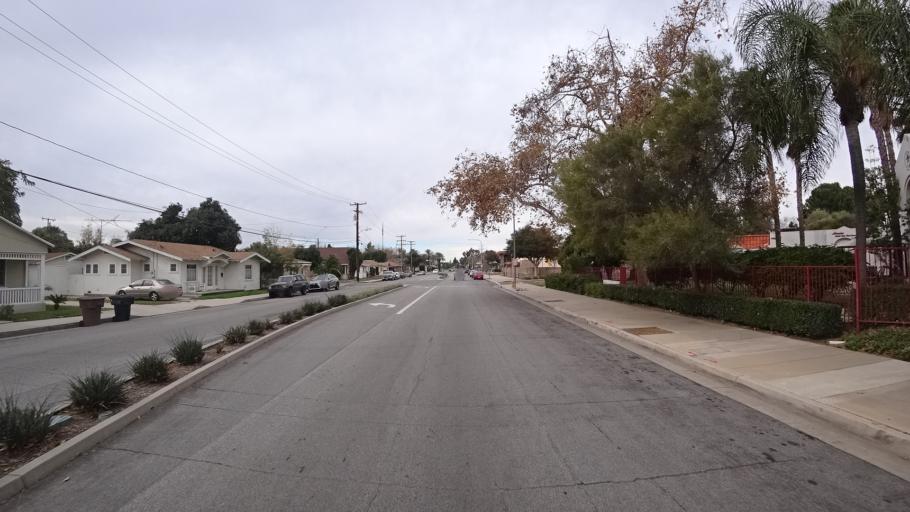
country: US
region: California
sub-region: Orange County
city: Garden Grove
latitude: 33.7761
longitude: -117.9339
